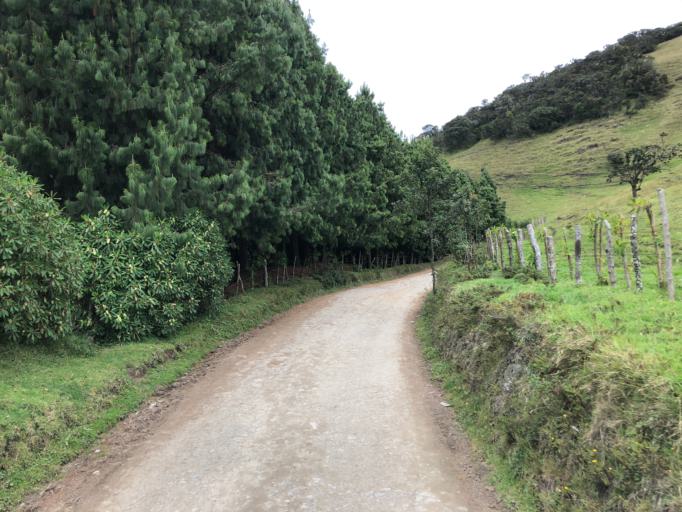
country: CO
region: Cauca
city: Totoro
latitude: 2.4742
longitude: -76.3464
